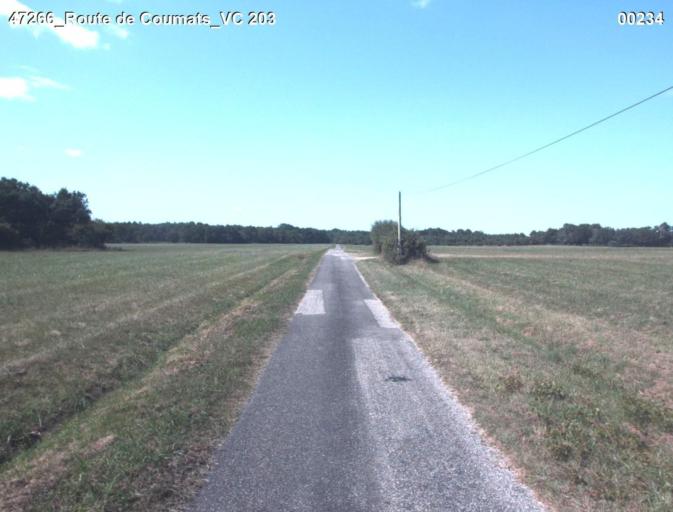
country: FR
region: Aquitaine
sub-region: Departement des Landes
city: Gabarret
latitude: 44.0155
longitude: 0.0889
